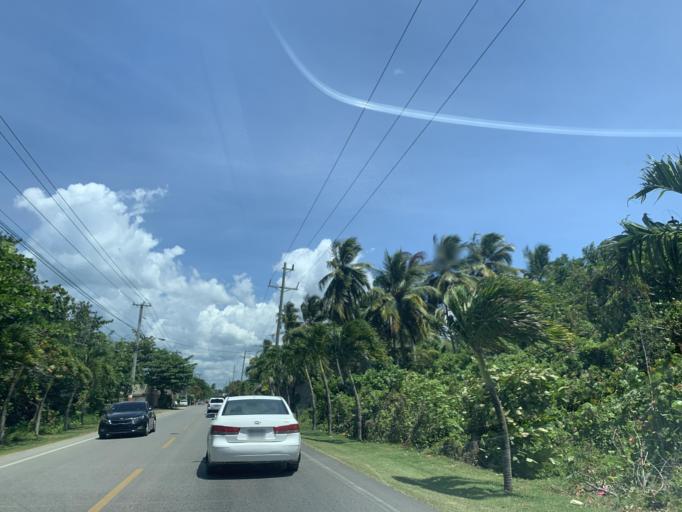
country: DO
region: Puerto Plata
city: Cabarete
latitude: 19.7408
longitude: -70.3924
